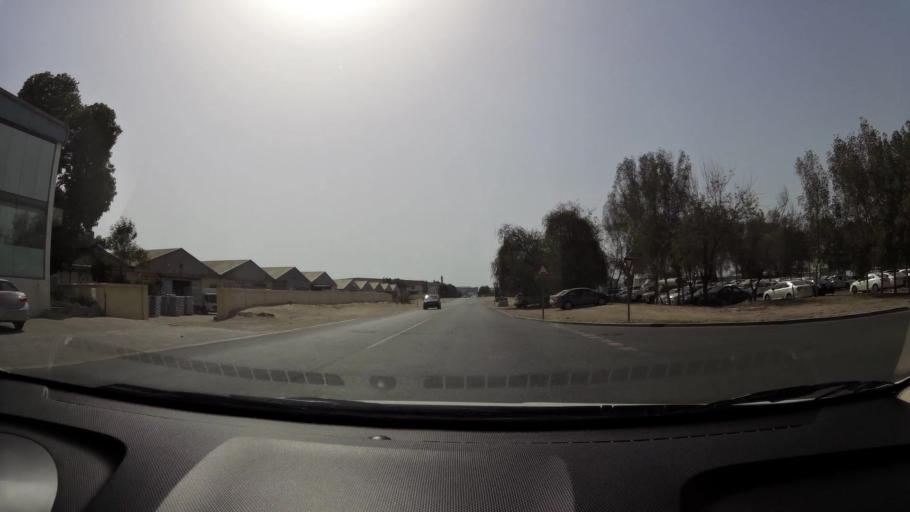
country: AE
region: Ash Shariqah
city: Sharjah
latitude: 25.2313
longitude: 55.3703
